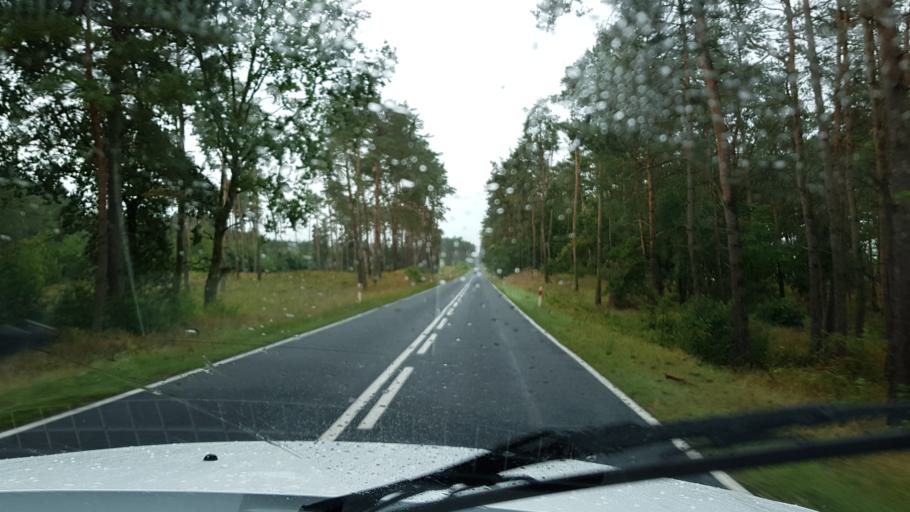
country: DE
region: Brandenburg
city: Schwedt (Oder)
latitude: 53.0491
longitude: 14.3434
